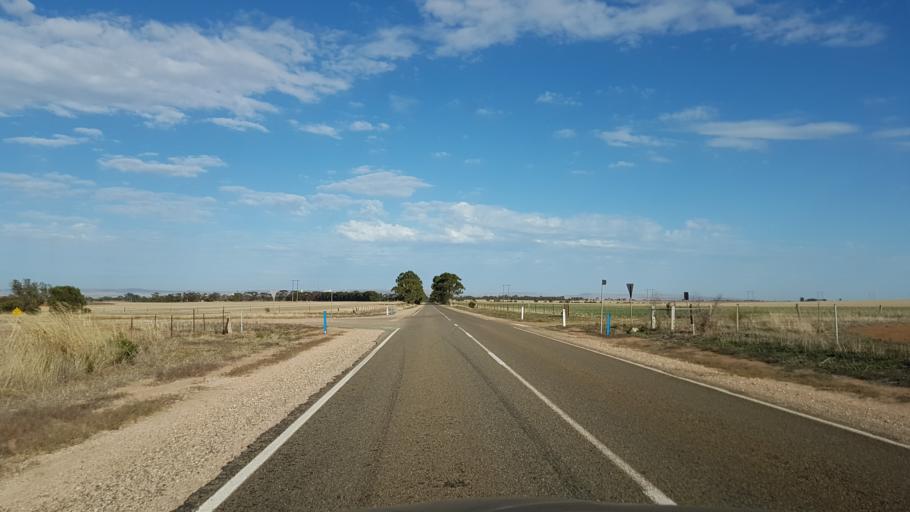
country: AU
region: South Australia
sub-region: Clare and Gilbert Valleys
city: Clare
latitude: -33.6953
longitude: 138.4326
